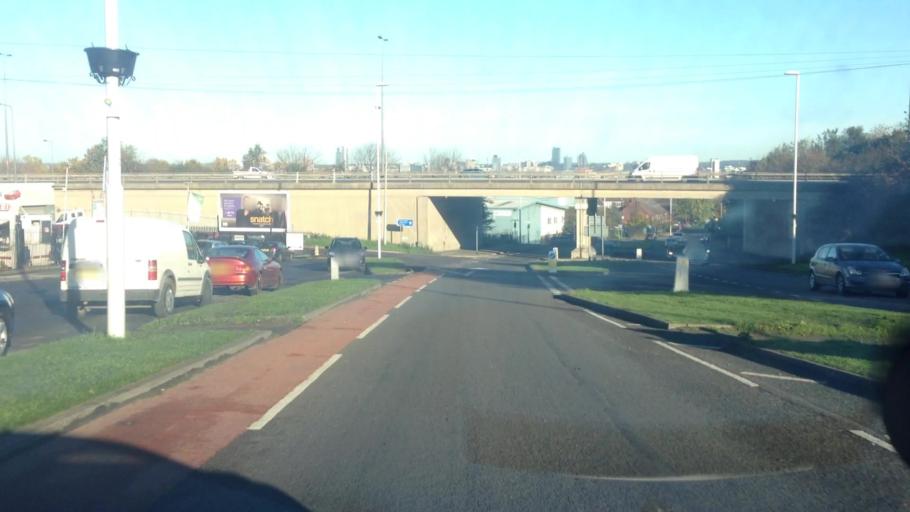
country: GB
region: England
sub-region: City and Borough of Leeds
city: Leeds
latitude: 53.7697
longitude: -1.5307
